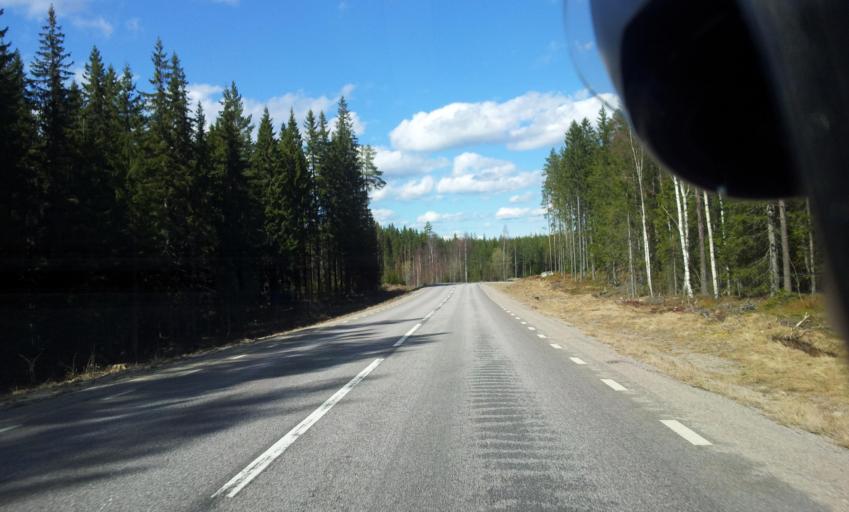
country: SE
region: Gaevleborg
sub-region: Bollnas Kommun
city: Vittsjo
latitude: 61.1443
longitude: 15.8860
